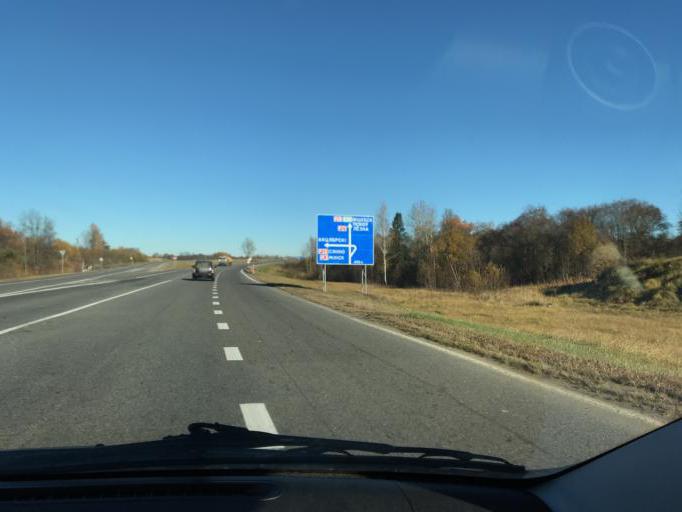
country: BY
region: Vitebsk
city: Vitebsk
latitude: 55.0962
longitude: 30.3014
